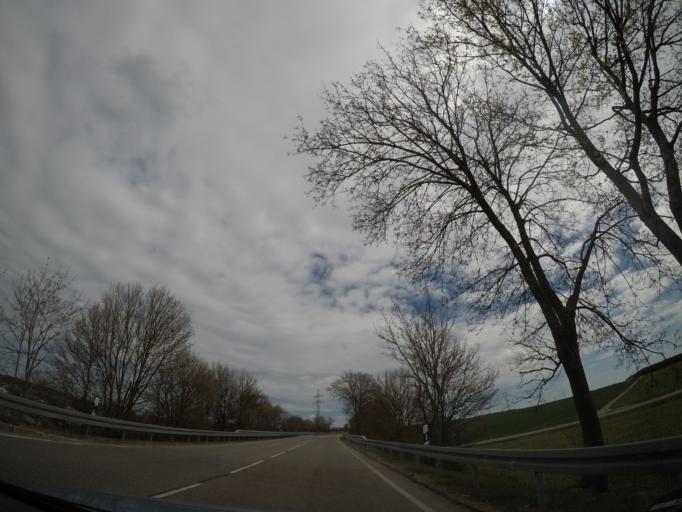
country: DE
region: Baden-Wuerttemberg
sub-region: Tuebingen Region
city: Laichingen
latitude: 48.4591
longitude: 9.7007
